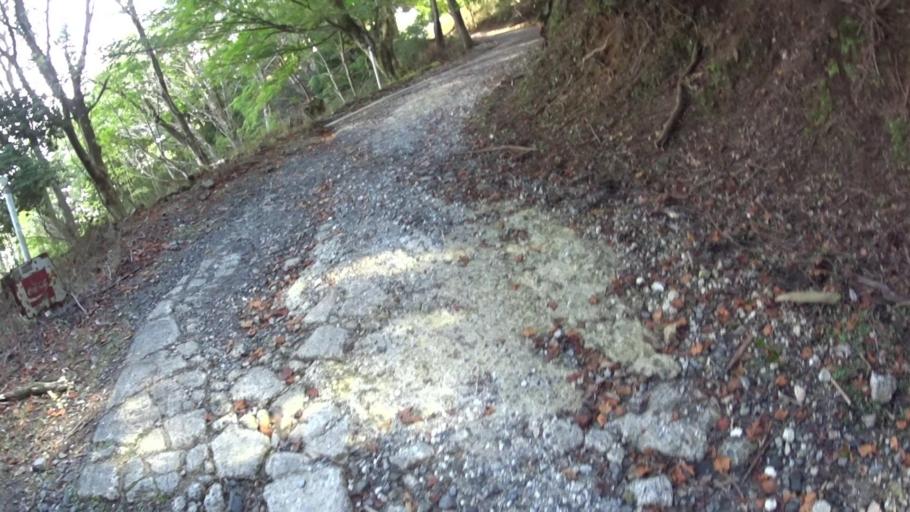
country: JP
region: Shiga Prefecture
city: Otsu-shi
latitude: 35.0659
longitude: 135.8249
